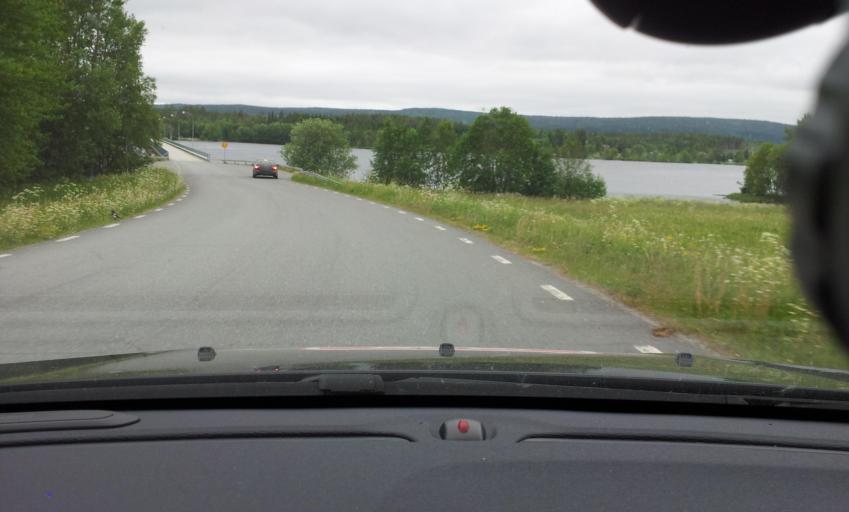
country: SE
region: Jaemtland
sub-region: Are Kommun
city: Jarpen
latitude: 63.3086
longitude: 13.6509
